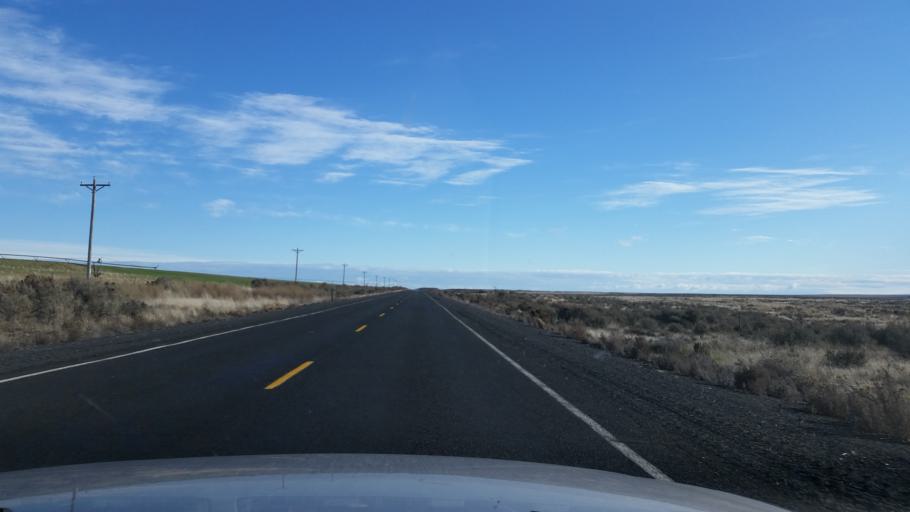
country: US
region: Washington
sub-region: Grant County
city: Warden
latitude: 47.3369
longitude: -118.8974
